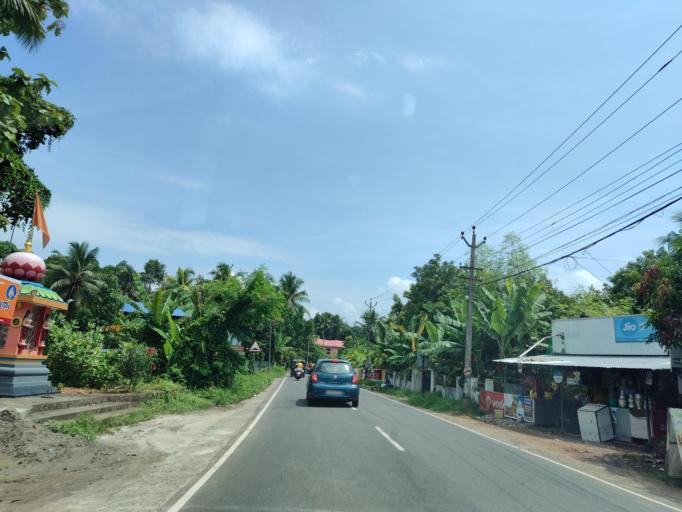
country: IN
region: Kerala
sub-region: Alappuzha
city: Chengannur
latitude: 9.3085
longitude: 76.5955
